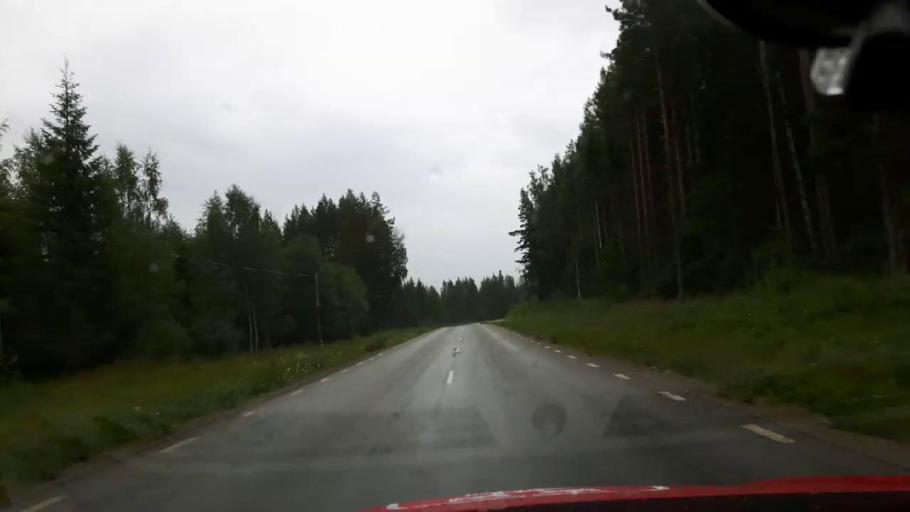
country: SE
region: Jaemtland
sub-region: OEstersunds Kommun
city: Brunflo
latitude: 62.8335
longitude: 15.0072
